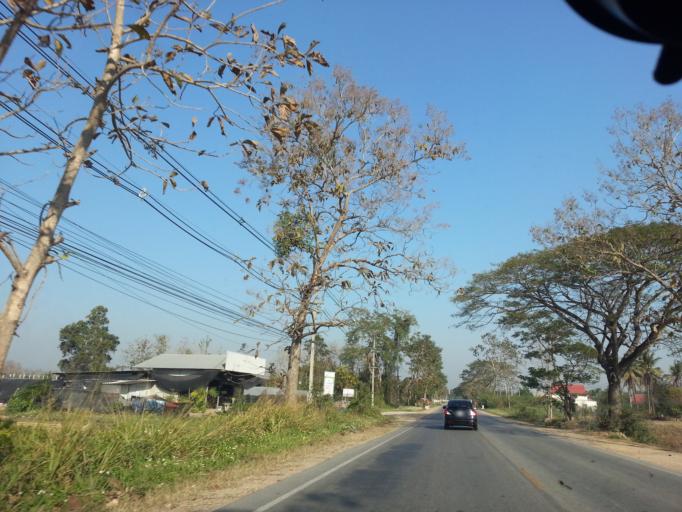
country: TH
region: Chiang Mai
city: San Sai
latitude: 18.9373
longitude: 98.9870
